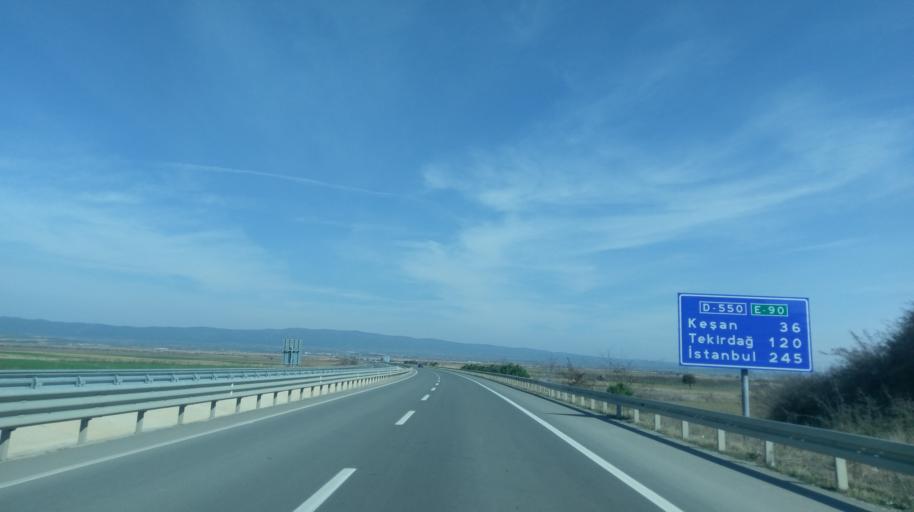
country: TR
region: Canakkale
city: Evrese
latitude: 40.6060
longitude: 26.8641
